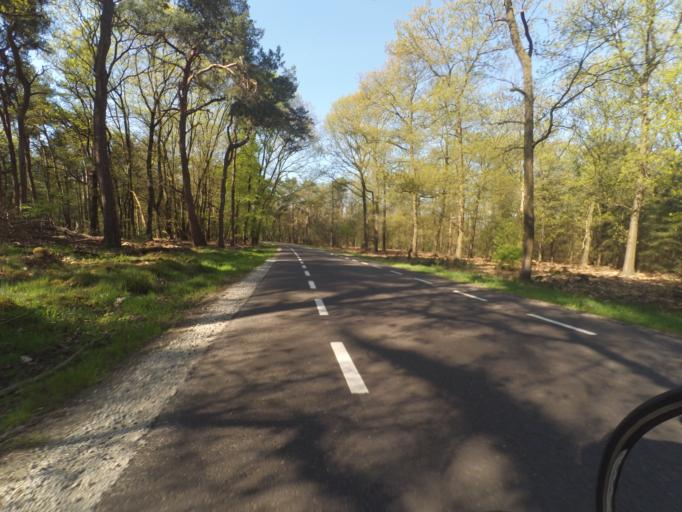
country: NL
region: Gelderland
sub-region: Gemeente Ede
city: Harskamp
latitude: 52.1748
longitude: 5.7469
